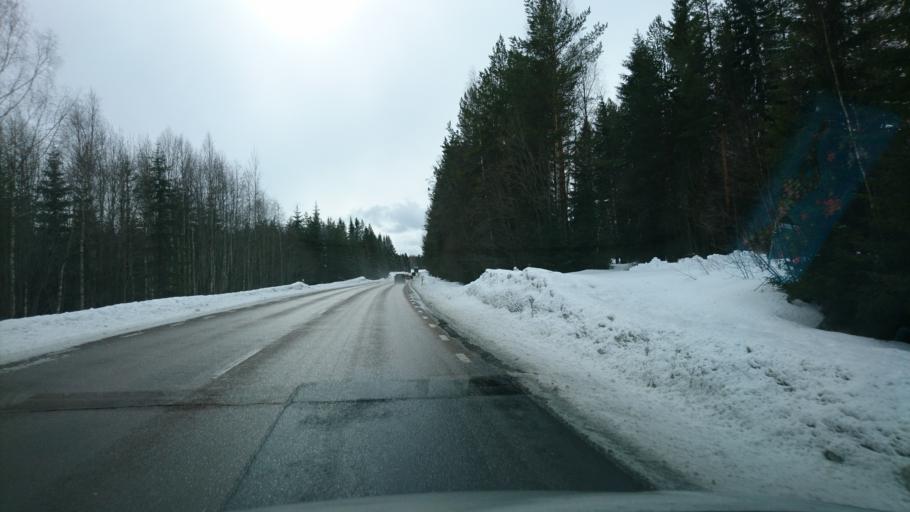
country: SE
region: Vaesternorrland
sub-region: Solleftea Kommun
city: Solleftea
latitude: 63.0858
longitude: 17.0140
